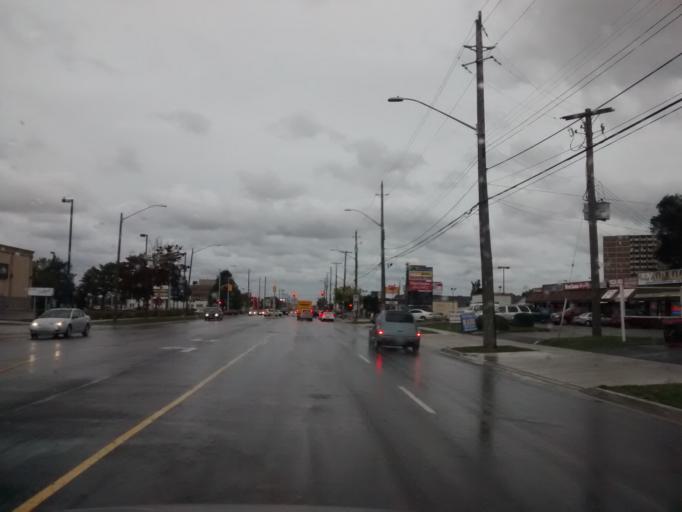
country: CA
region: Ontario
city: Hamilton
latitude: 43.2310
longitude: -79.7630
